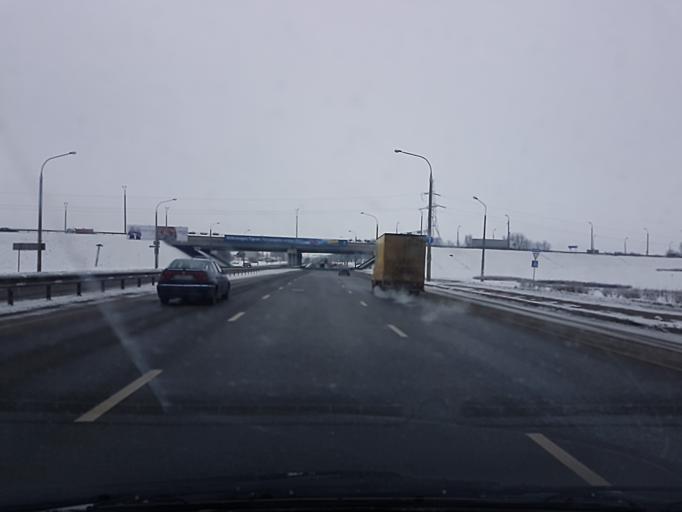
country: BY
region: Minsk
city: Shchomyslitsa
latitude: 53.8439
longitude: 27.4704
